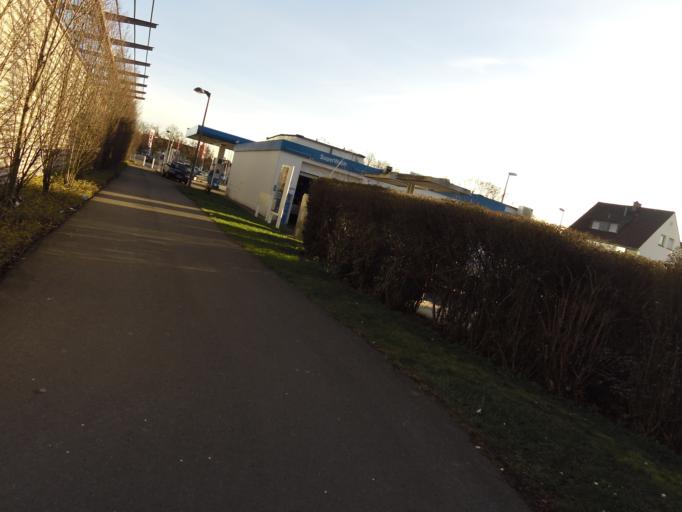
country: DE
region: Rheinland-Pfalz
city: Frankenthal
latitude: 49.5347
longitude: 8.3889
